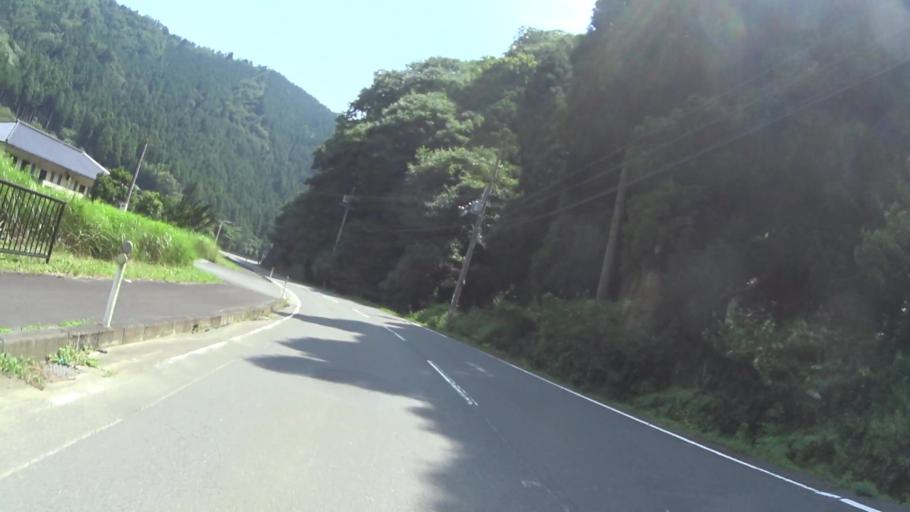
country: JP
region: Fukui
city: Obama
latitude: 35.3161
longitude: 135.5573
